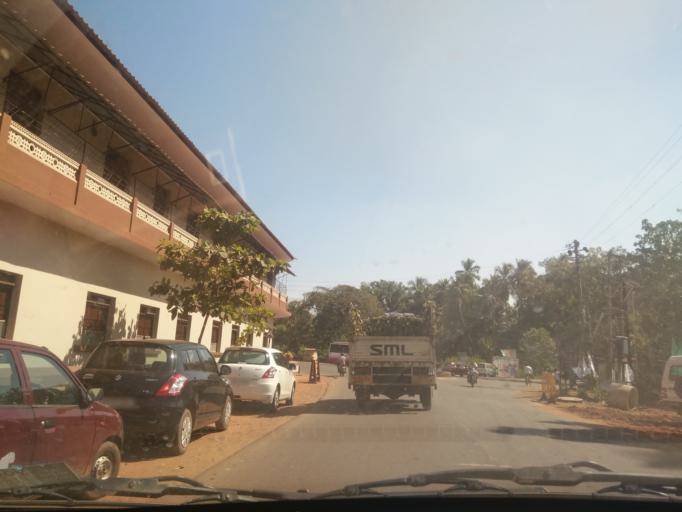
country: IN
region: Goa
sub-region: North Goa
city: Dicholi
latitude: 15.5916
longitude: 73.9461
